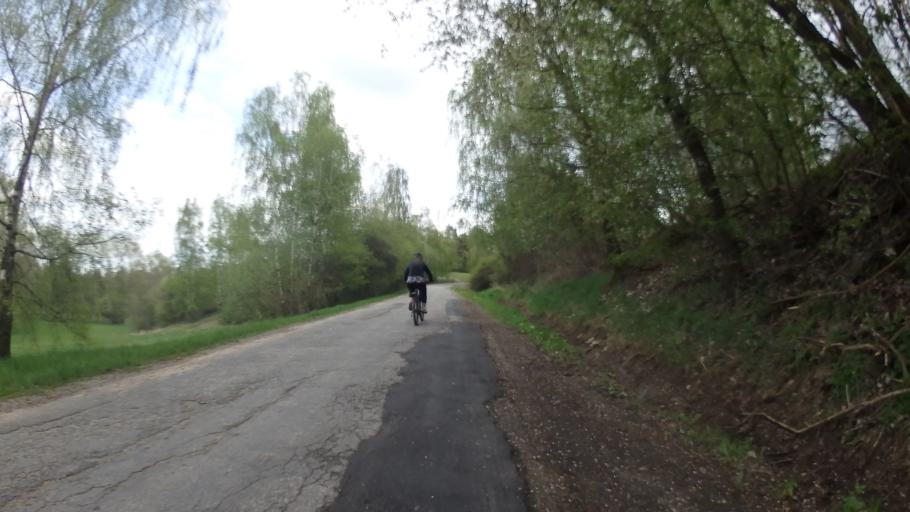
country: CZ
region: Vysocina
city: Merin
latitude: 49.3732
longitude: 15.8877
